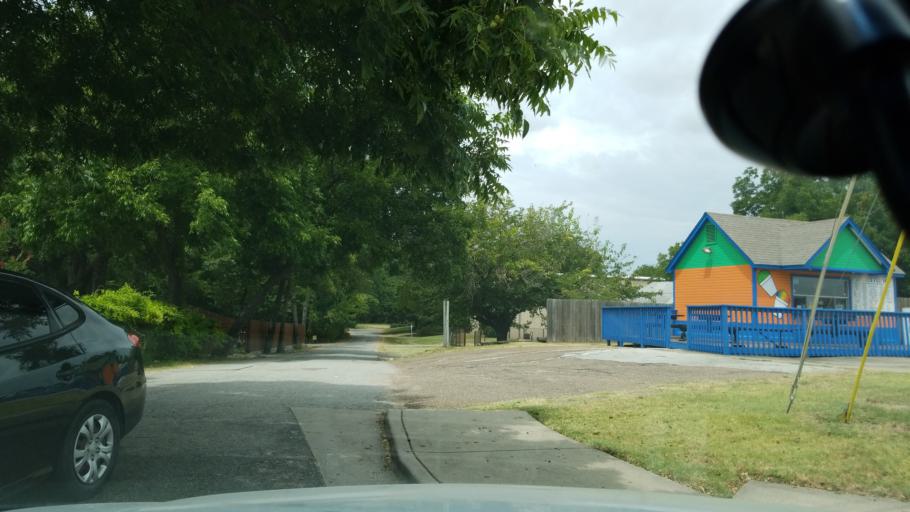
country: US
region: Texas
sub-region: Dallas County
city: Grand Prairie
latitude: 32.7365
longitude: -96.9951
